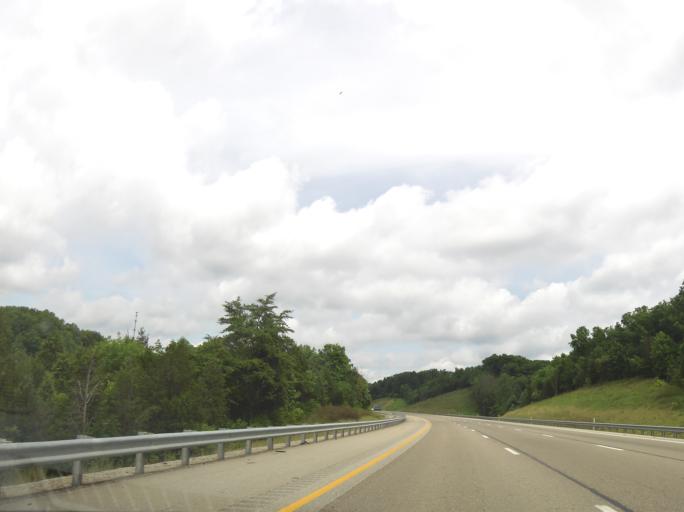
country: US
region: Kentucky
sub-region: Grant County
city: Williamstown
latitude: 38.4789
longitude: -84.5797
